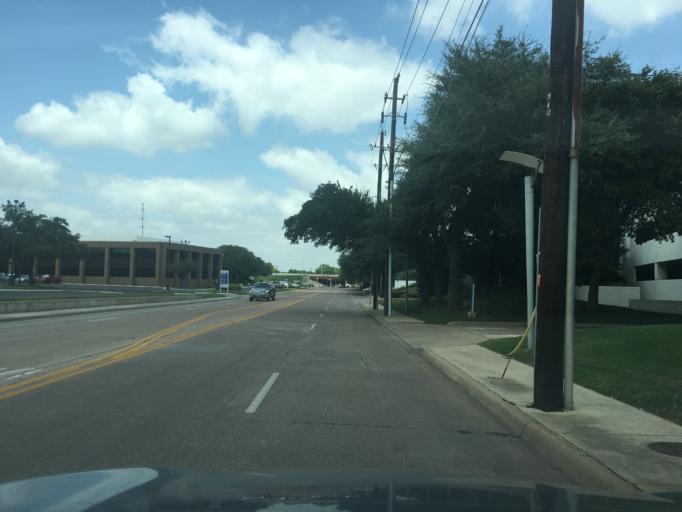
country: US
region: Texas
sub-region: Dallas County
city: Addison
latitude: 32.9229
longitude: -96.8156
